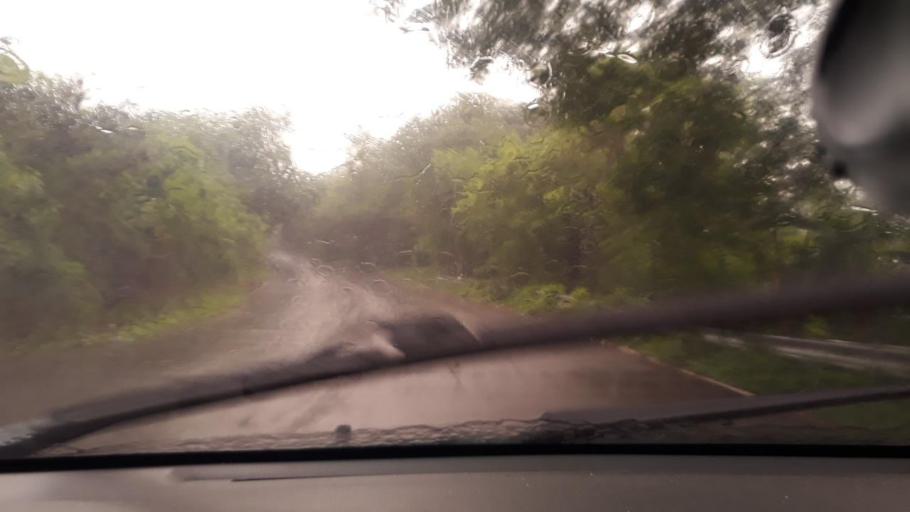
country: GT
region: Jutiapa
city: Comapa
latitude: 14.0425
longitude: -89.9168
